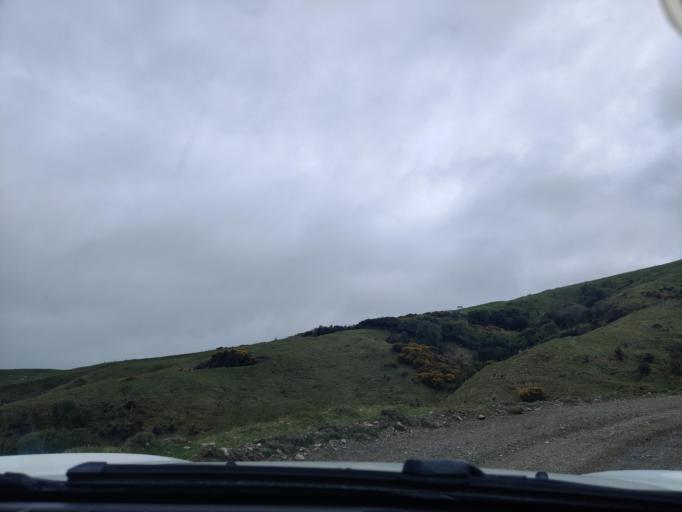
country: NZ
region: Manawatu-Wanganui
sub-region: Palmerston North City
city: Palmerston North
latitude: -40.2764
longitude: 175.8520
